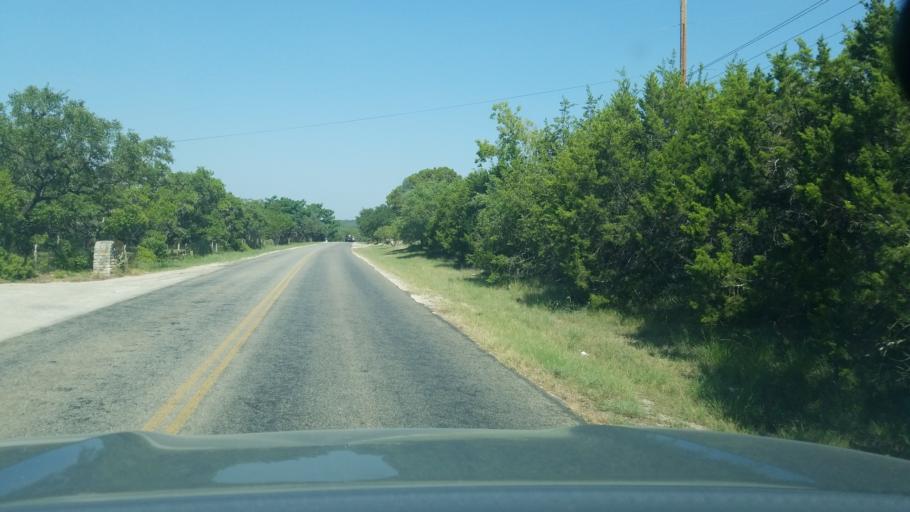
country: US
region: Texas
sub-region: Kendall County
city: Boerne
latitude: 29.7871
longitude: -98.6831
